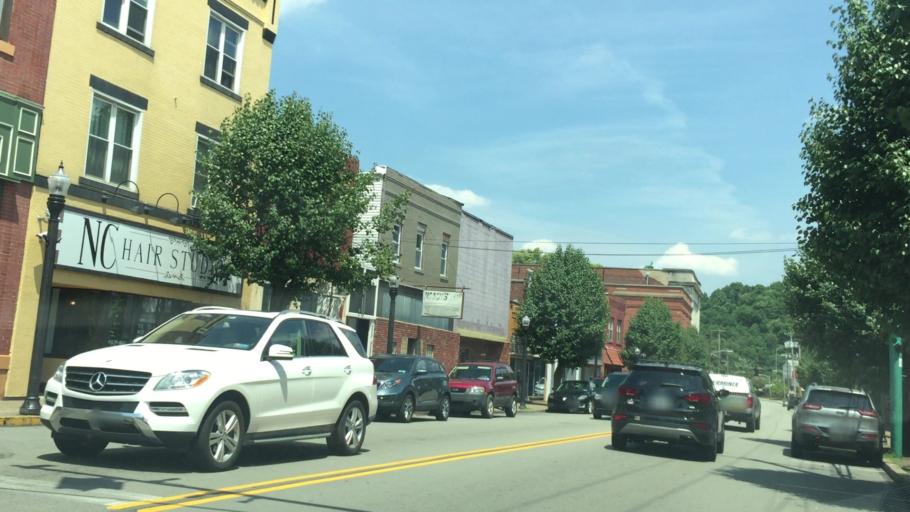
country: US
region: Pennsylvania
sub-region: Allegheny County
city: Etna
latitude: 40.4979
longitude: -79.9439
